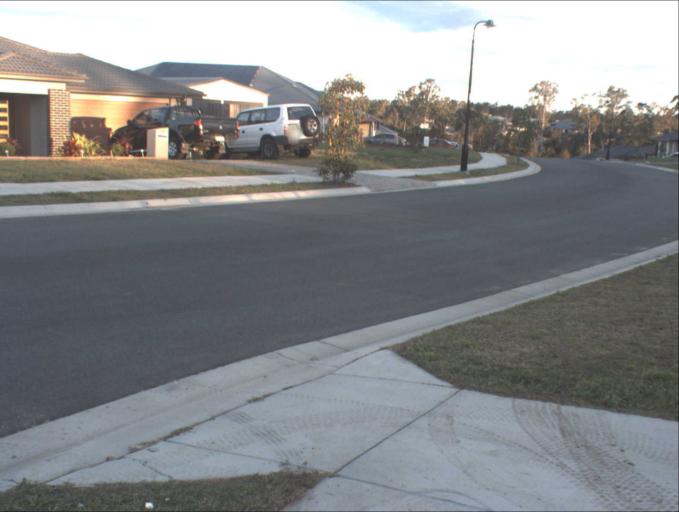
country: AU
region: Queensland
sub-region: Logan
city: North Maclean
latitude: -27.7998
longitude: 152.9542
